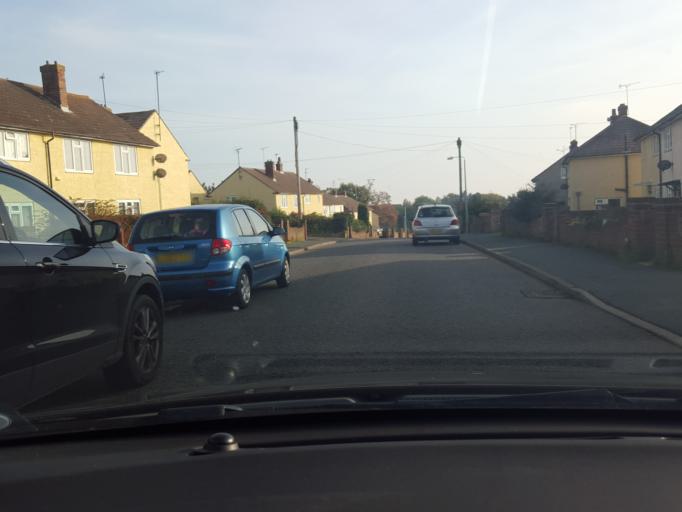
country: GB
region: England
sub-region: Essex
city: Dovercourt
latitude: 51.9323
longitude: 1.2545
